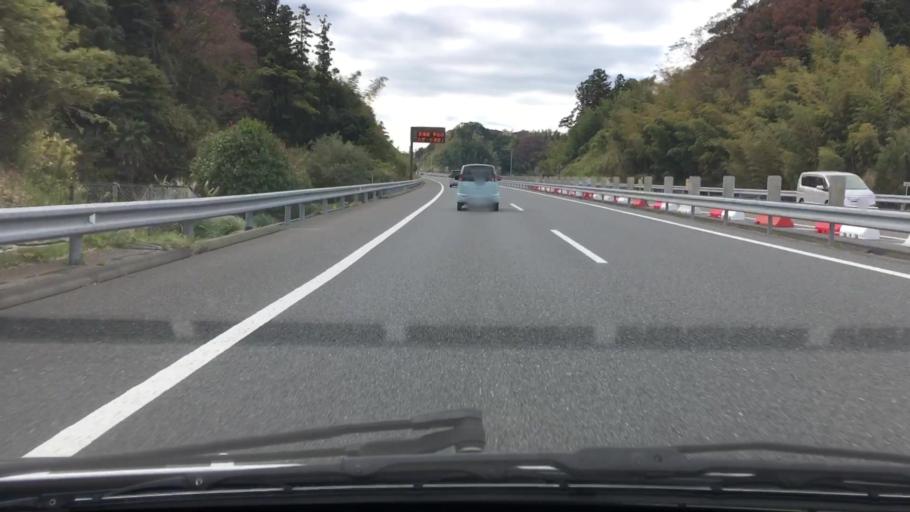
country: JP
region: Chiba
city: Kimitsu
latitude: 35.2582
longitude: 139.8951
